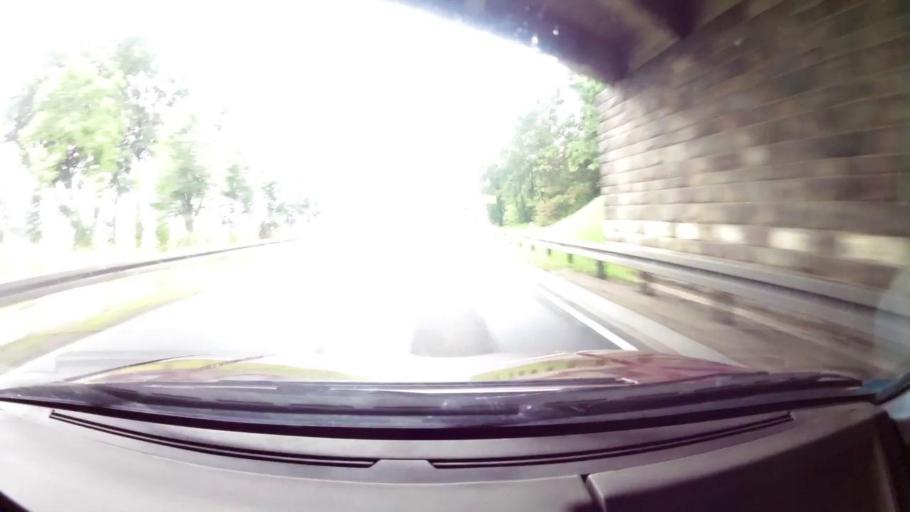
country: PL
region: West Pomeranian Voivodeship
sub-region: Powiat stargardzki
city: Chociwel
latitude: 53.4331
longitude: 15.2953
